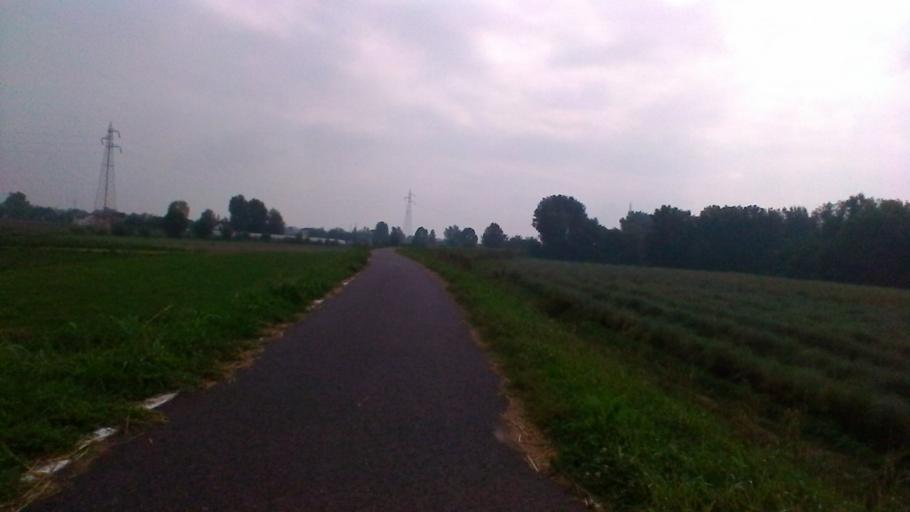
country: IT
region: Veneto
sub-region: Provincia di Verona
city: San Giovanni Lupatoto
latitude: 45.4094
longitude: 11.0270
